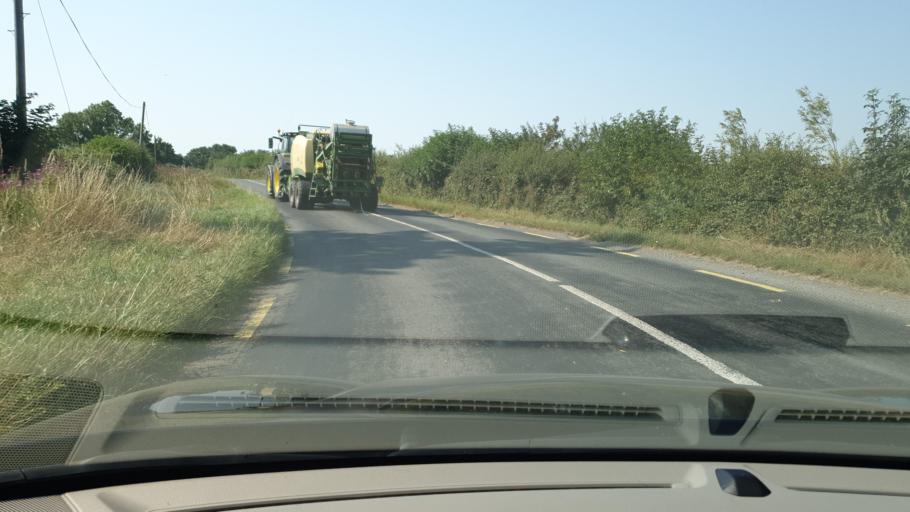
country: IE
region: Leinster
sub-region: An Mhi
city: Athboy
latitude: 53.5901
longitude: -6.8577
